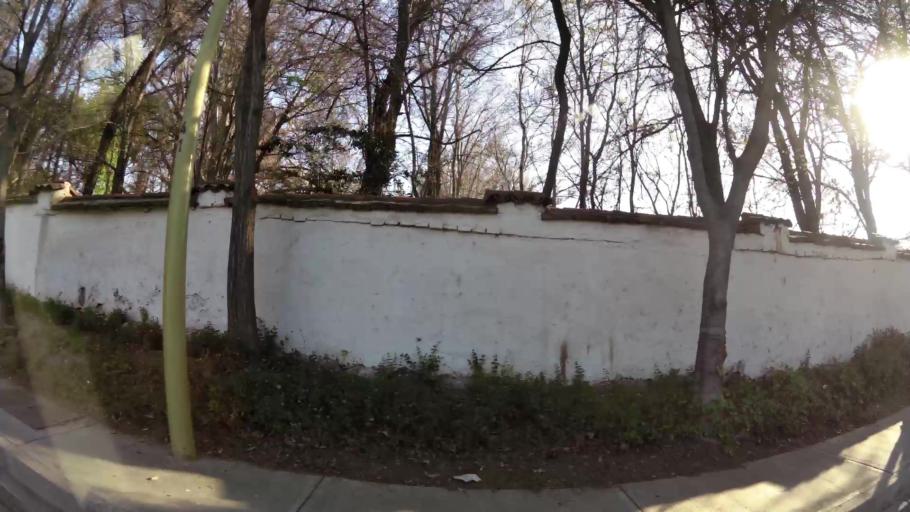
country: CL
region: Santiago Metropolitan
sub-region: Provincia de Santiago
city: Villa Presidente Frei, Nunoa, Santiago, Chile
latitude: -33.3858
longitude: -70.5272
